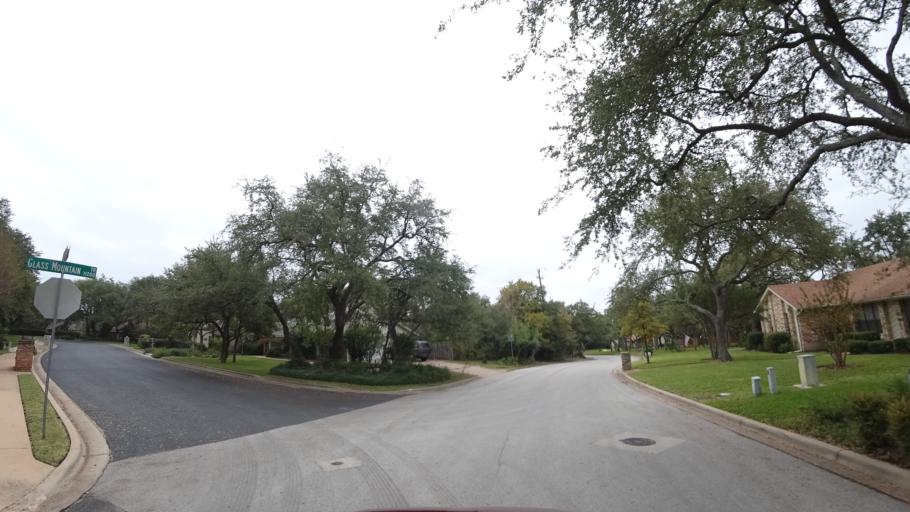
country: US
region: Texas
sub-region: Williamson County
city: Anderson Mill
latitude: 30.4438
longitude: -97.8137
